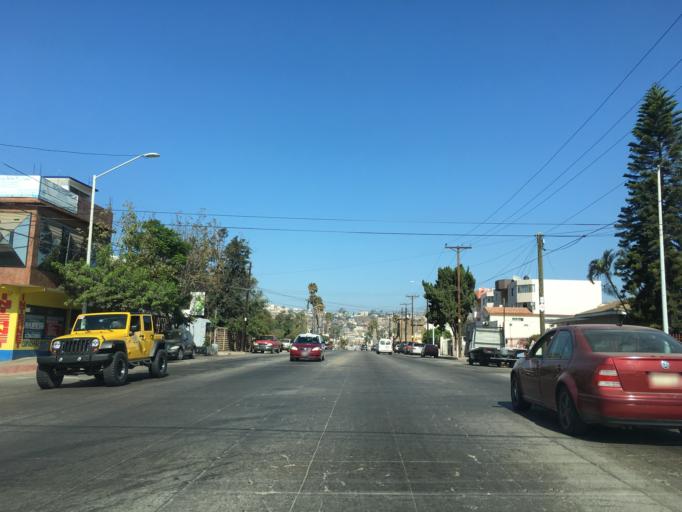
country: MX
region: Baja California
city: Ensenada
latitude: 31.8616
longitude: -116.6127
